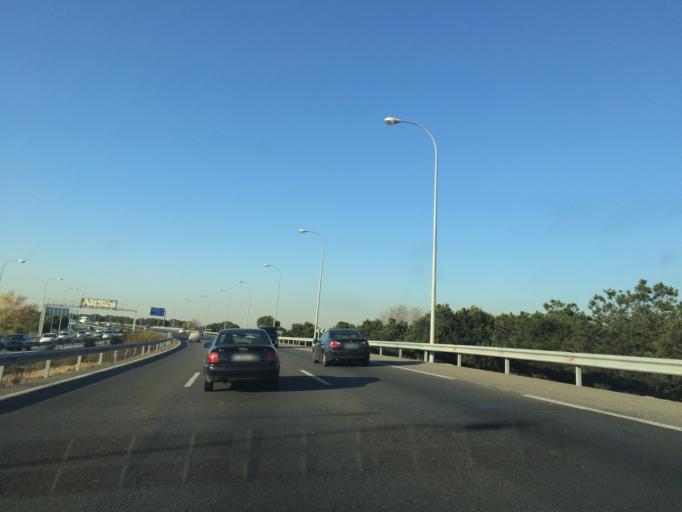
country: ES
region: Madrid
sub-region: Provincia de Madrid
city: Alcorcon
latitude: 40.3786
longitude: -3.8093
